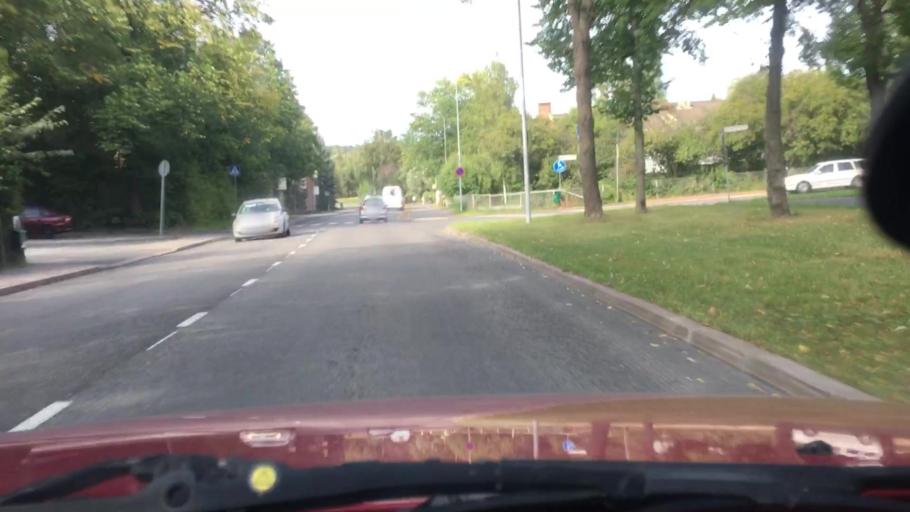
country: FI
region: Varsinais-Suomi
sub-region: Turku
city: Turku
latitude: 60.4578
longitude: 22.2461
